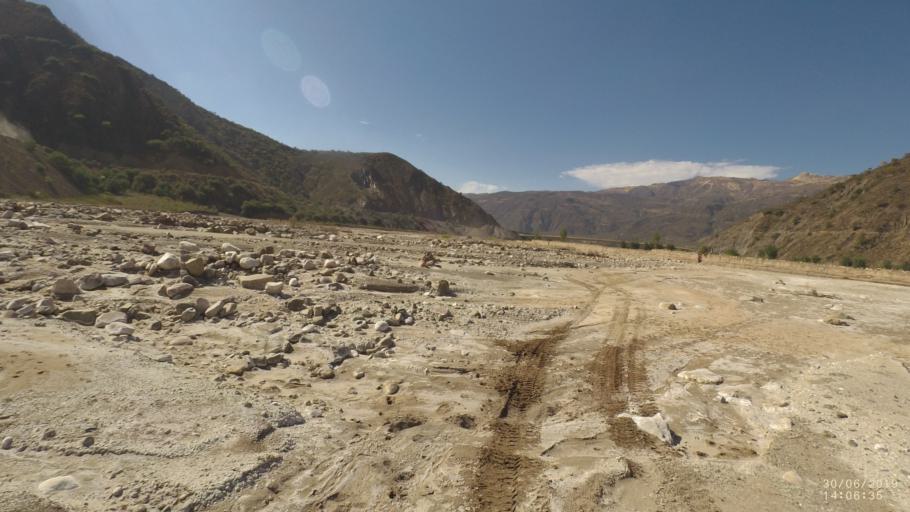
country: BO
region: Cochabamba
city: Irpa Irpa
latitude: -17.8033
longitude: -66.3554
